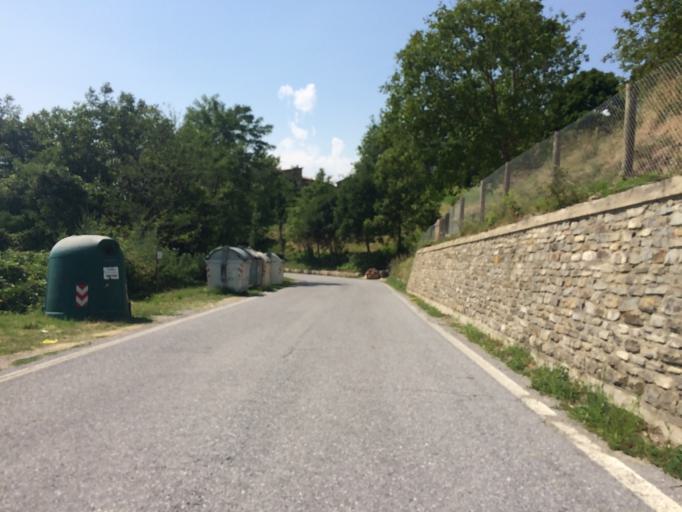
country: IT
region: Piedmont
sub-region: Provincia di Cuneo
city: Serravalle Langhe
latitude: 44.5593
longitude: 8.0579
